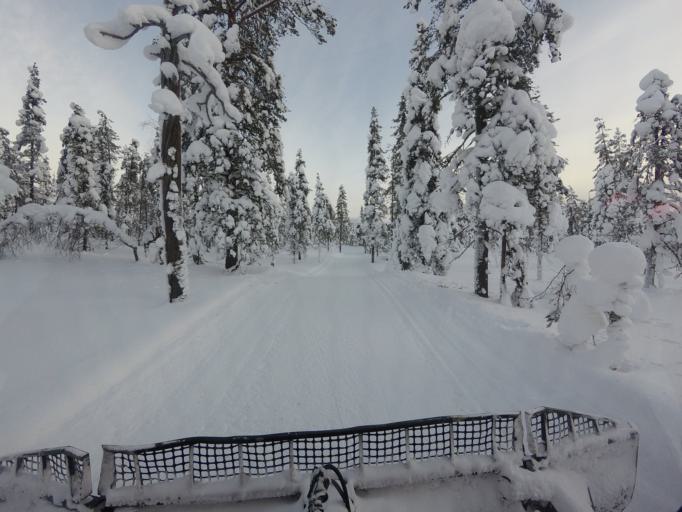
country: FI
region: Lapland
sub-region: Tunturi-Lappi
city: Kolari
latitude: 67.6548
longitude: 24.2485
